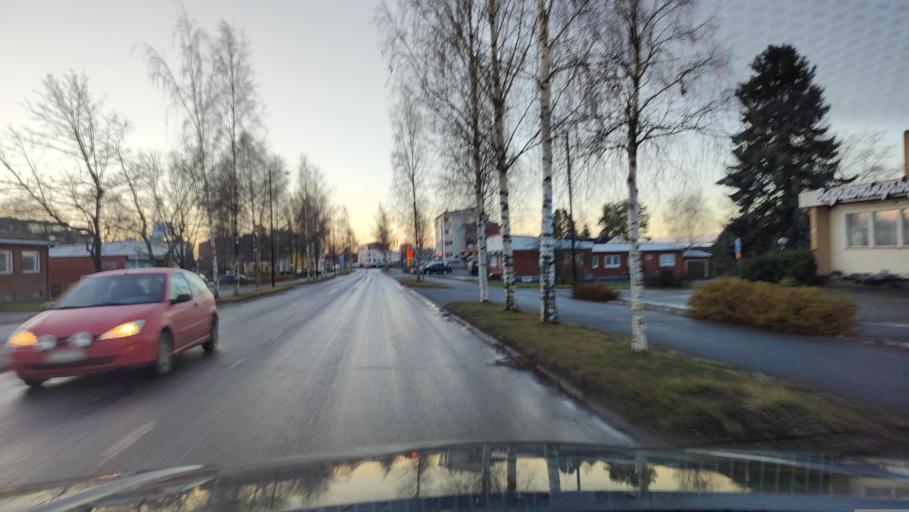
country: FI
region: Ostrobothnia
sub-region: Sydosterbotten
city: Naerpes
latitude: 62.4811
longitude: 21.3380
